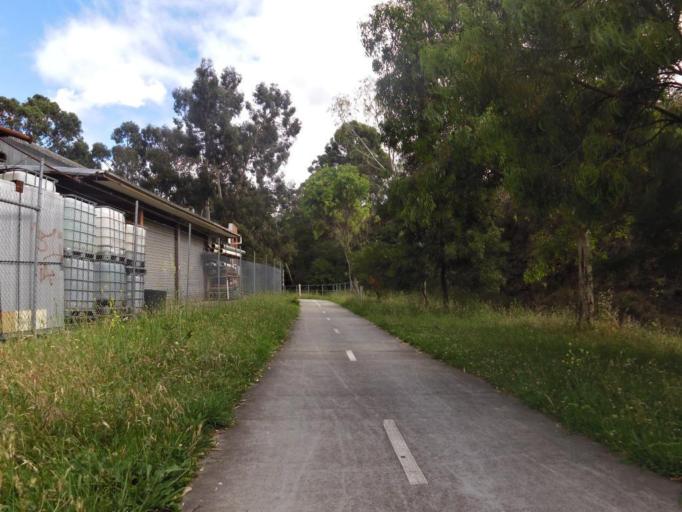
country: AU
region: Victoria
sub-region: Banyule
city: Bellfield
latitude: -37.7655
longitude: 145.0308
